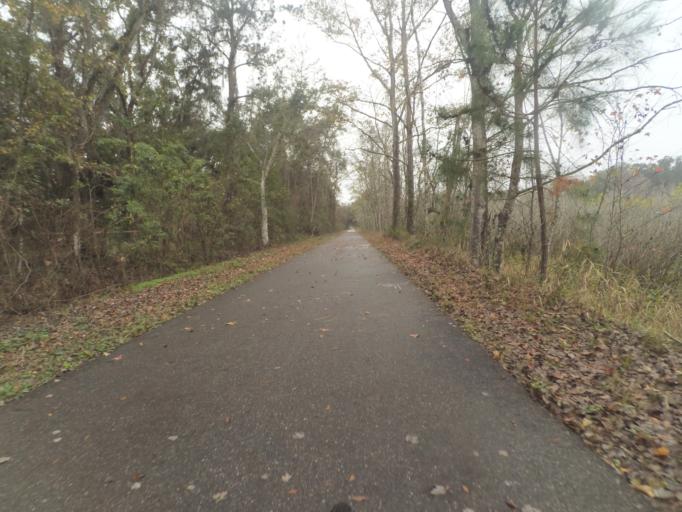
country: US
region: Florida
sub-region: Alachua County
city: Hawthorne
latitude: 29.5992
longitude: -82.1553
